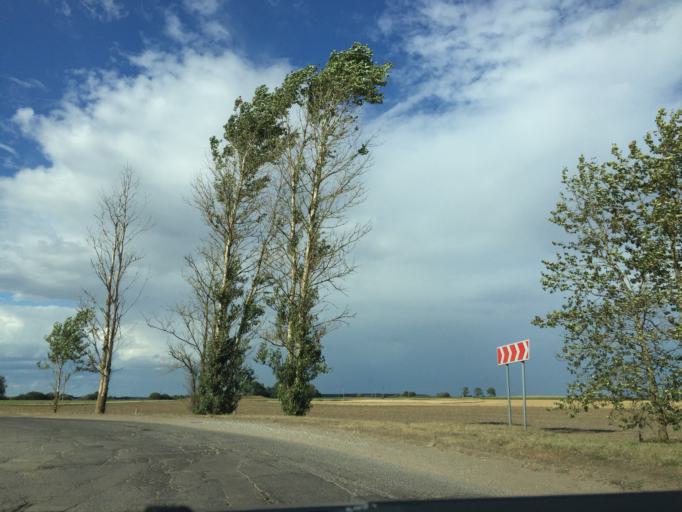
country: LV
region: Tervete
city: Zelmeni
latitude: 56.2987
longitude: 23.4079
